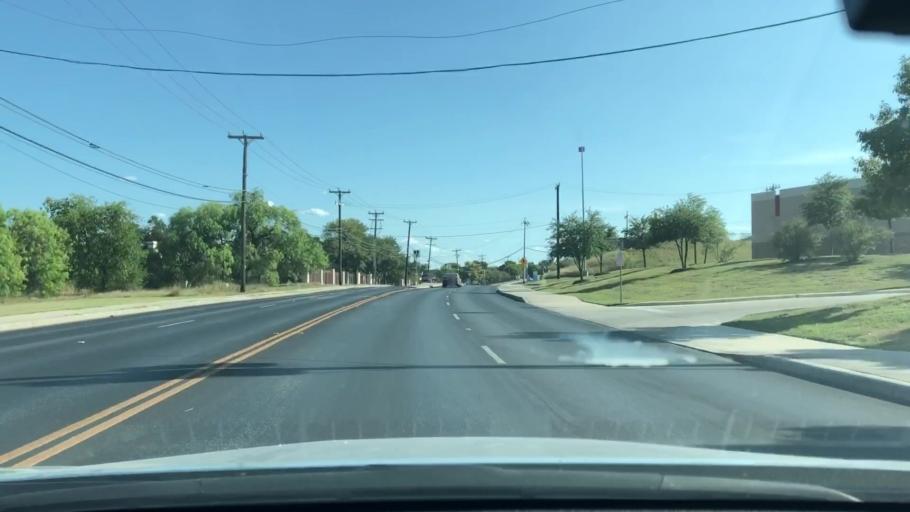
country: US
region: Texas
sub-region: Bexar County
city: Kirby
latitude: 29.4836
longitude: -98.3472
